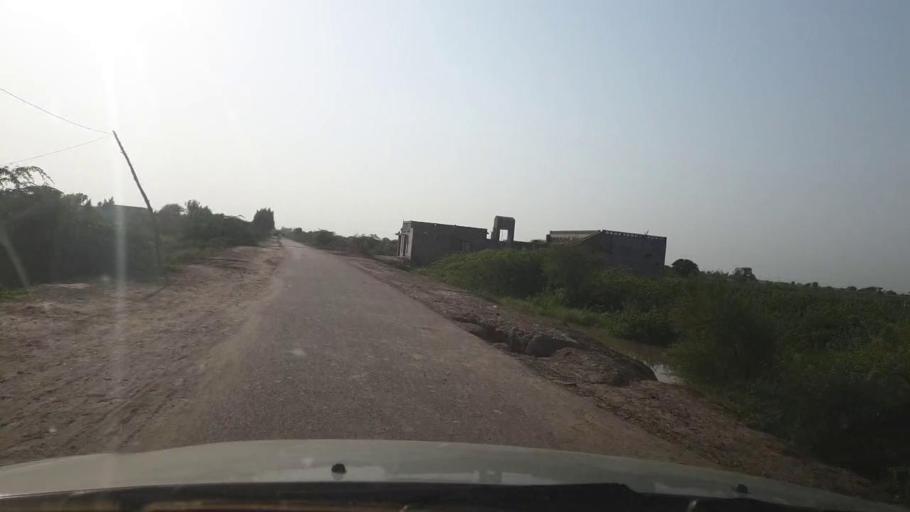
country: PK
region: Sindh
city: Tando Ghulam Ali
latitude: 25.1834
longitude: 68.9470
